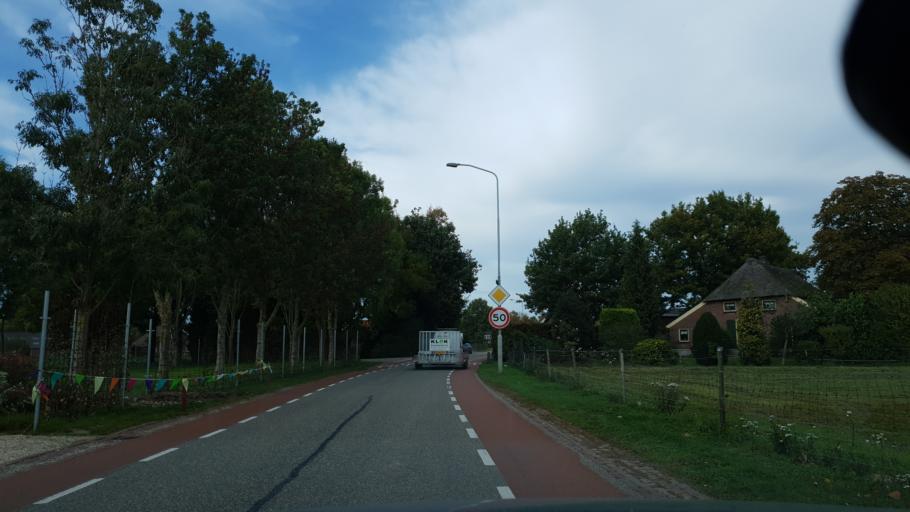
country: NL
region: Gelderland
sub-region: Gemeente Wijchen
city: Bergharen
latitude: 51.8593
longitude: 5.6550
